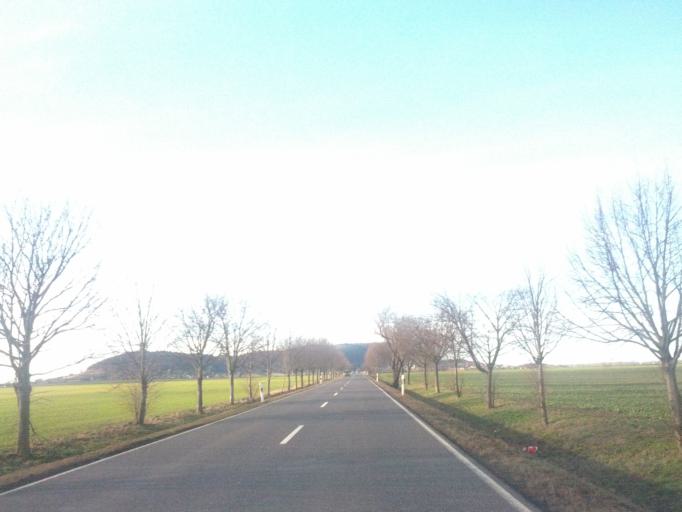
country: DE
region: Thuringia
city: Wandersleben
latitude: 50.9095
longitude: 10.8273
